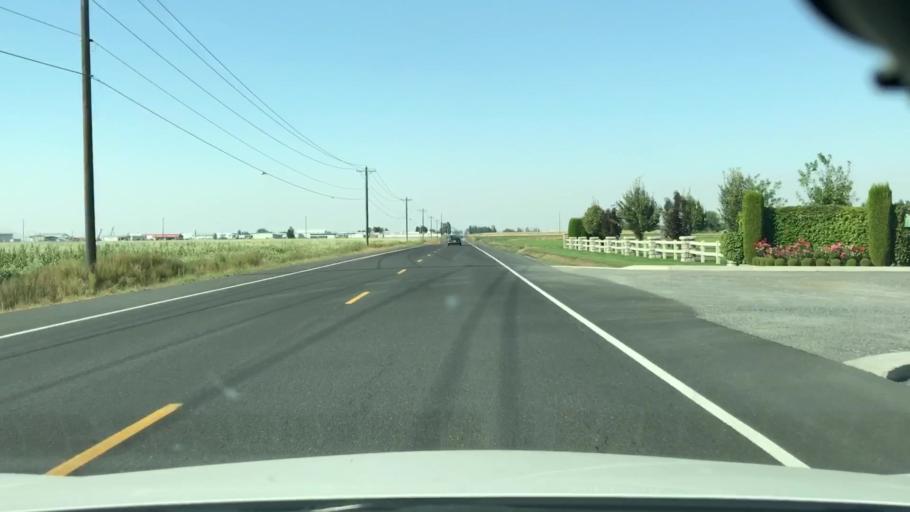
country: US
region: Washington
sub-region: Grant County
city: Moses Lake
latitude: 47.1249
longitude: -119.2358
